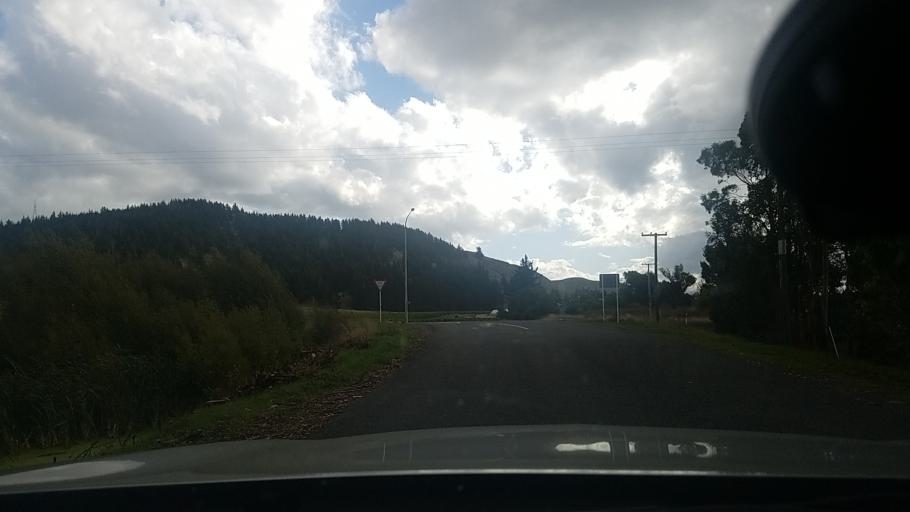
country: NZ
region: Marlborough
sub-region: Marlborough District
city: Blenheim
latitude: -41.5456
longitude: 174.0421
